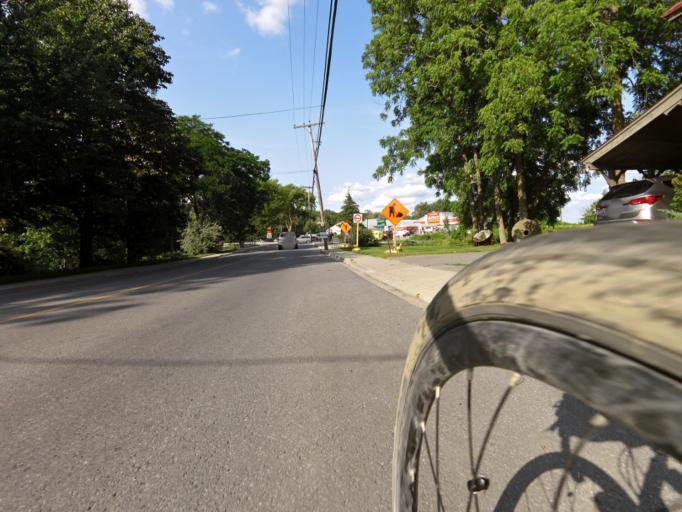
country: CA
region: Ontario
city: Kingston
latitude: 44.4129
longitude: -76.5949
